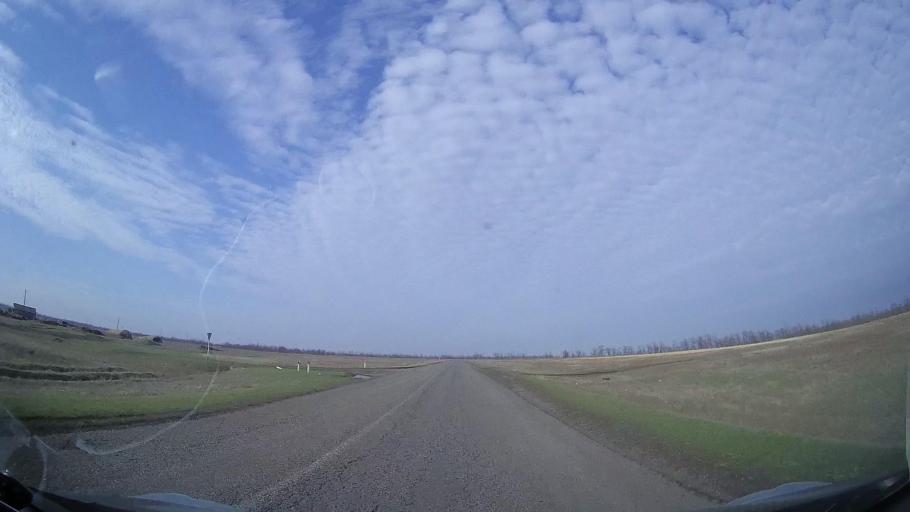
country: RU
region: Rostov
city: Gigant
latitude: 46.8484
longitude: 41.3236
